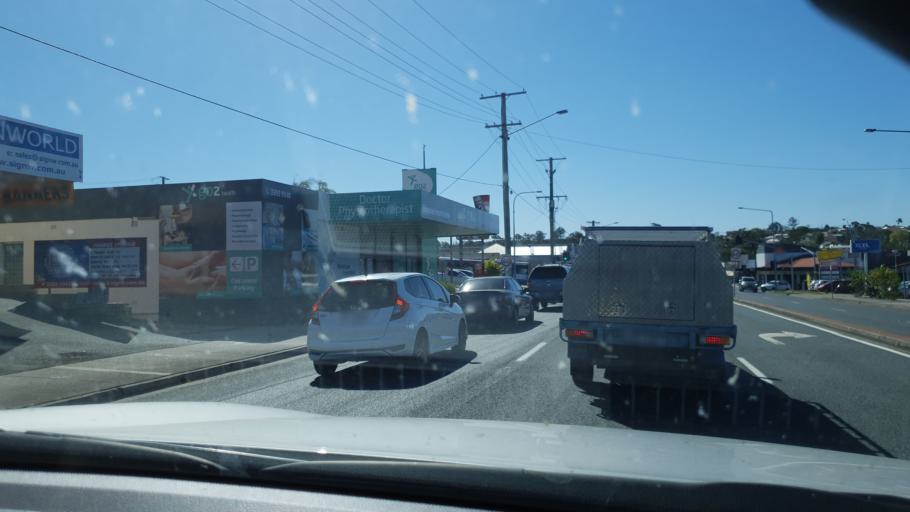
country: AU
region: Queensland
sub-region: Brisbane
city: Everton Park
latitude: -27.4084
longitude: 152.9910
